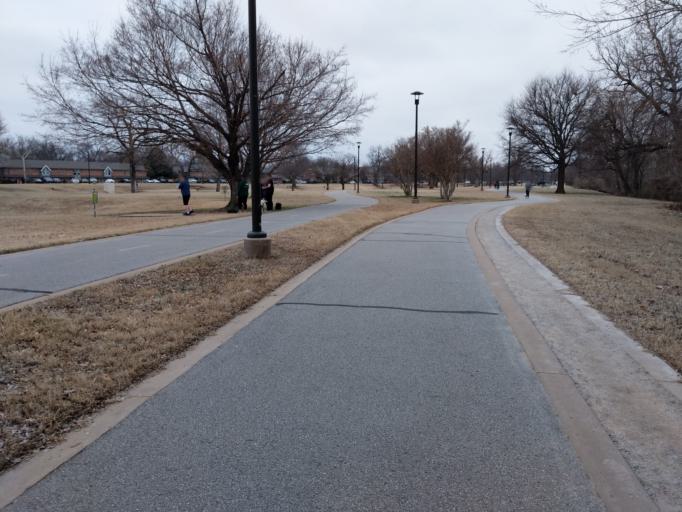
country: US
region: Oklahoma
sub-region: Tulsa County
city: Tulsa
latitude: 36.1085
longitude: -95.9842
